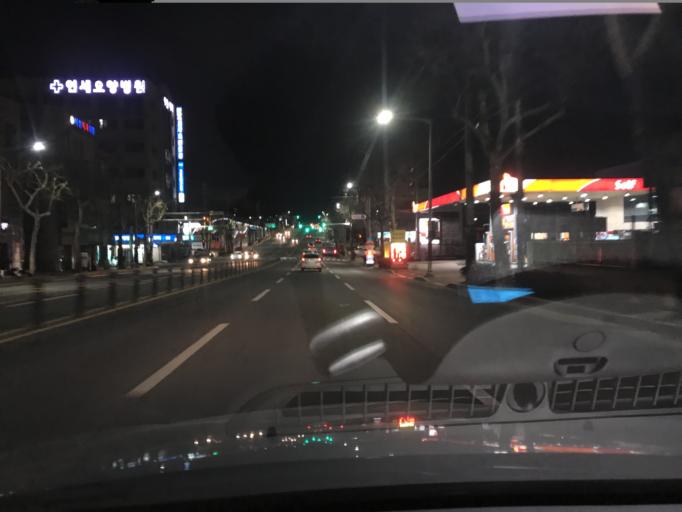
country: KR
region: Daegu
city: Daegu
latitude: 35.8789
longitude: 128.5516
